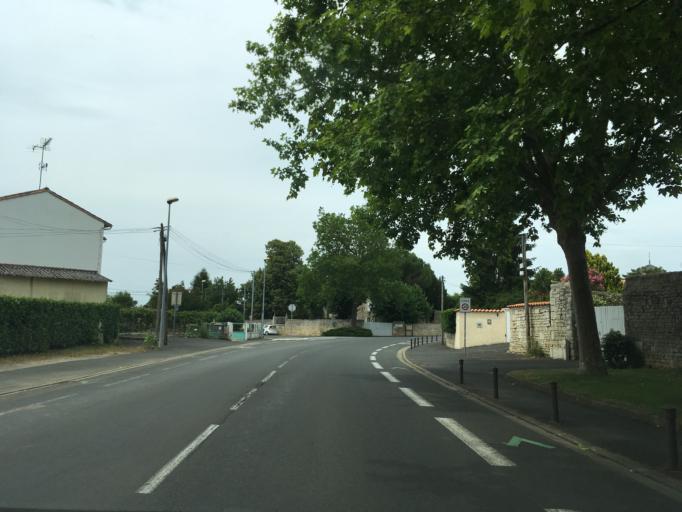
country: FR
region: Poitou-Charentes
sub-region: Departement des Deux-Sevres
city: Bessines
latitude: 46.3237
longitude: -0.5128
